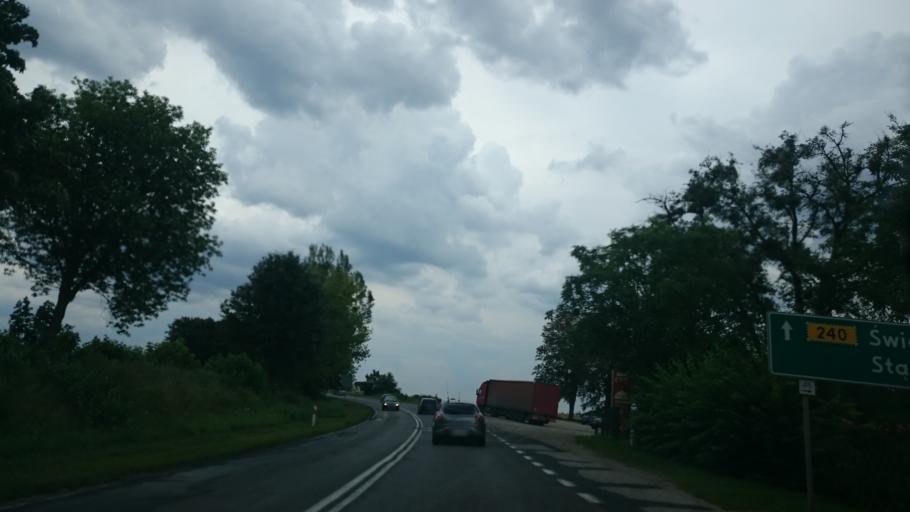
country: PL
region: Kujawsko-Pomorskie
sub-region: Powiat tucholski
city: Cekcyn
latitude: 53.5178
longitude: 17.9534
